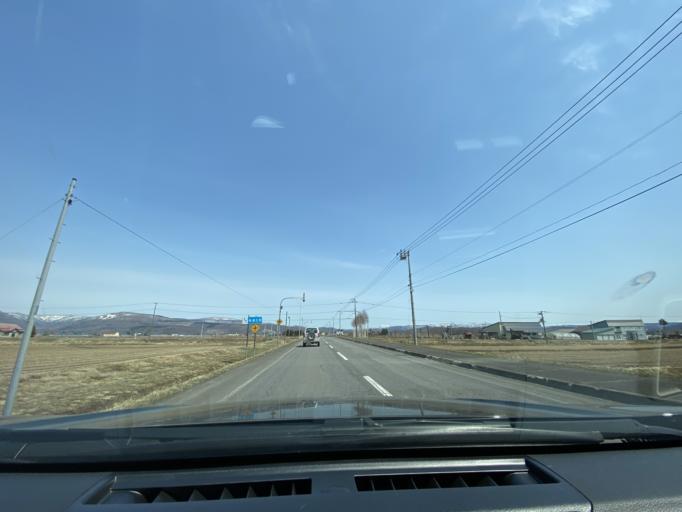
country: JP
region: Hokkaido
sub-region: Asahikawa-shi
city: Asahikawa
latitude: 43.8758
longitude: 142.4947
